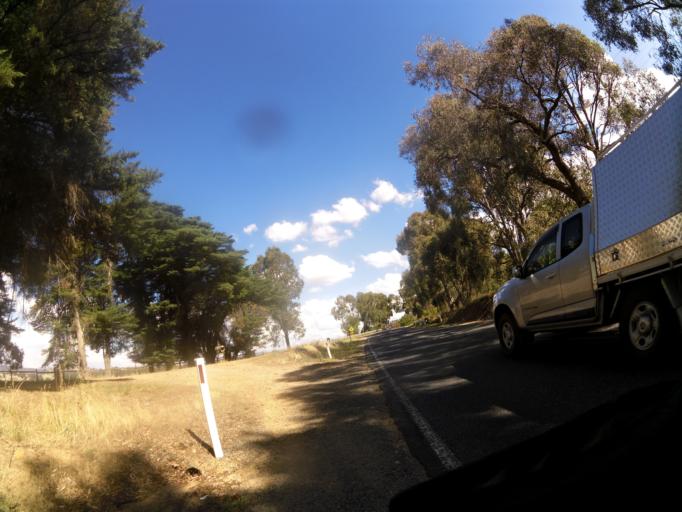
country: AU
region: Victoria
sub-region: Mansfield
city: Mansfield
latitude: -36.9244
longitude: 146.0018
